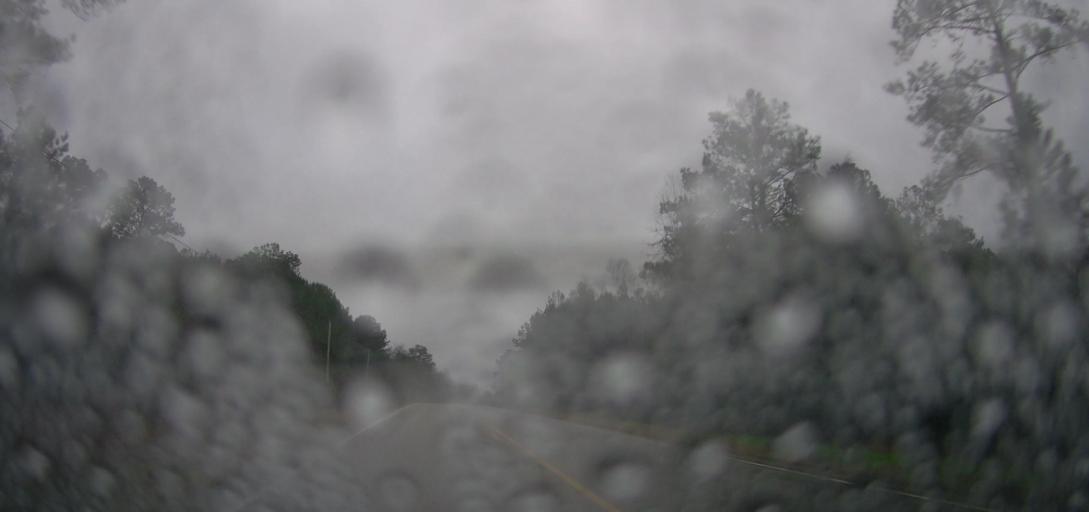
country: US
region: Alabama
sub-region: Autauga County
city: Pine Level
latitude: 32.5204
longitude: -86.6083
